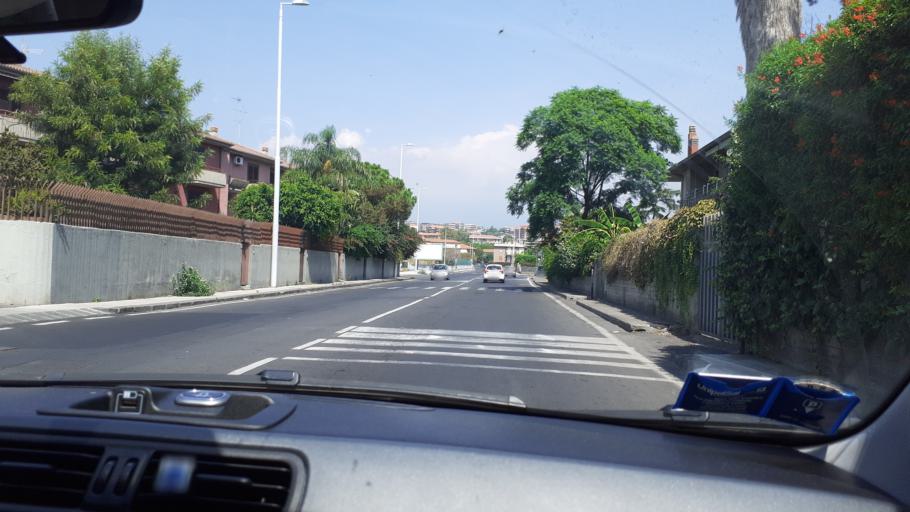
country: IT
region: Sicily
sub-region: Catania
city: Misterbianco
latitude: 37.5144
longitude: 15.0562
